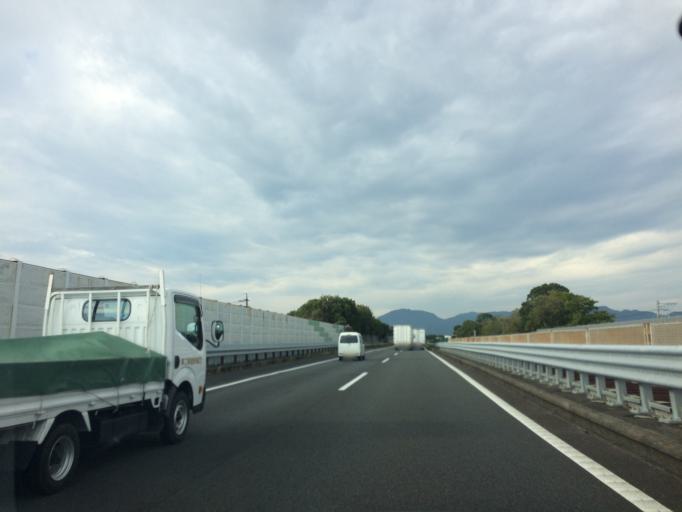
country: JP
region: Shizuoka
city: Shizuoka-shi
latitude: 34.9546
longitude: 138.4115
